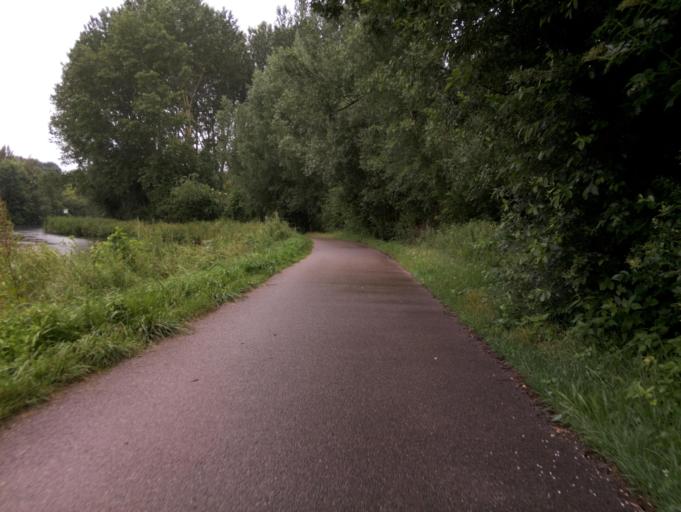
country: FR
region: Picardie
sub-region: Departement de la Somme
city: Dreuil-les-Amiens
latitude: 49.9214
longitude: 2.2150
